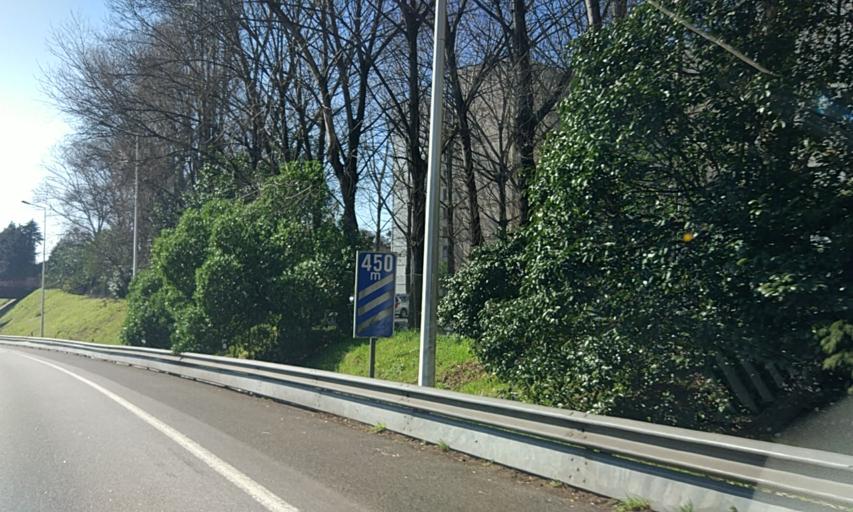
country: PT
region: Porto
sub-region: Matosinhos
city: Senhora da Hora
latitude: 41.1717
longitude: -8.6294
